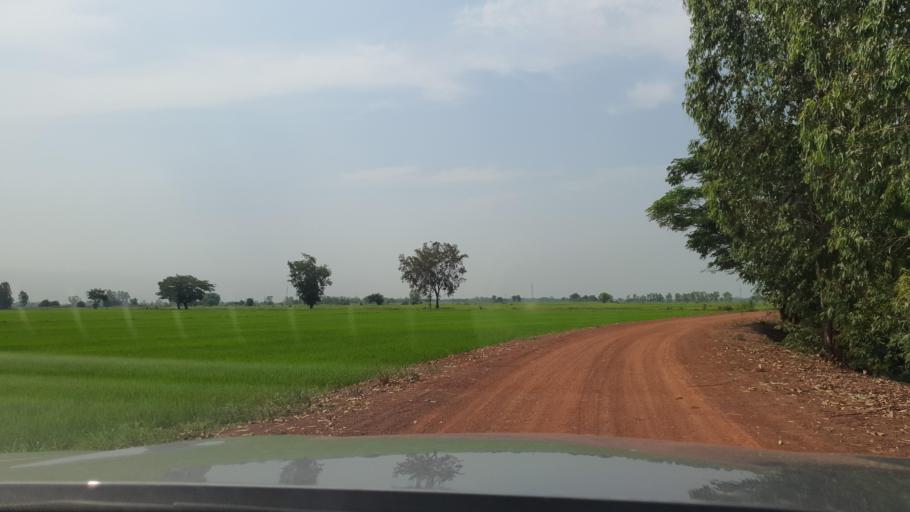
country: TH
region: Phitsanulok
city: Bang Rakam
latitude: 16.7956
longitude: 100.1080
